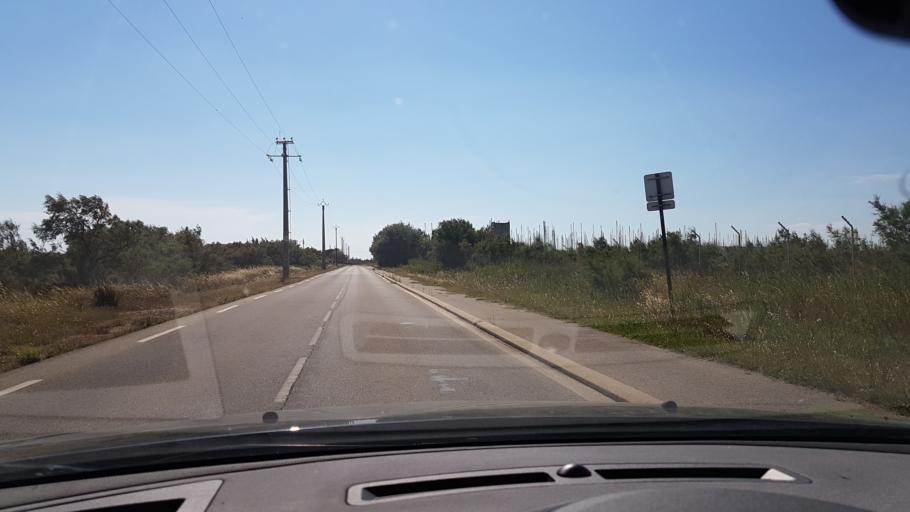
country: FR
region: Provence-Alpes-Cote d'Azur
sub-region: Departement des Bouches-du-Rhone
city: Port-Saint-Louis-du-Rhone
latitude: 43.3825
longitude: 4.8435
